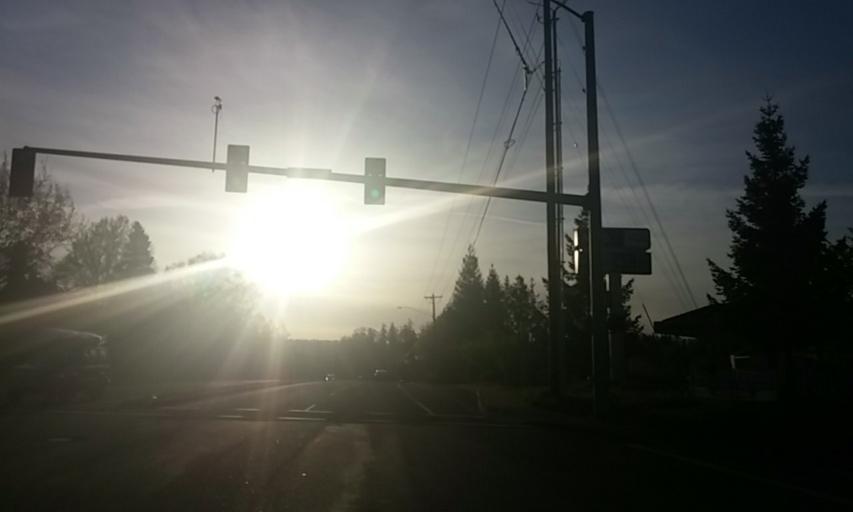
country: US
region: Oregon
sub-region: Washington County
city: Oak Hills
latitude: 45.5318
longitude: -122.8350
